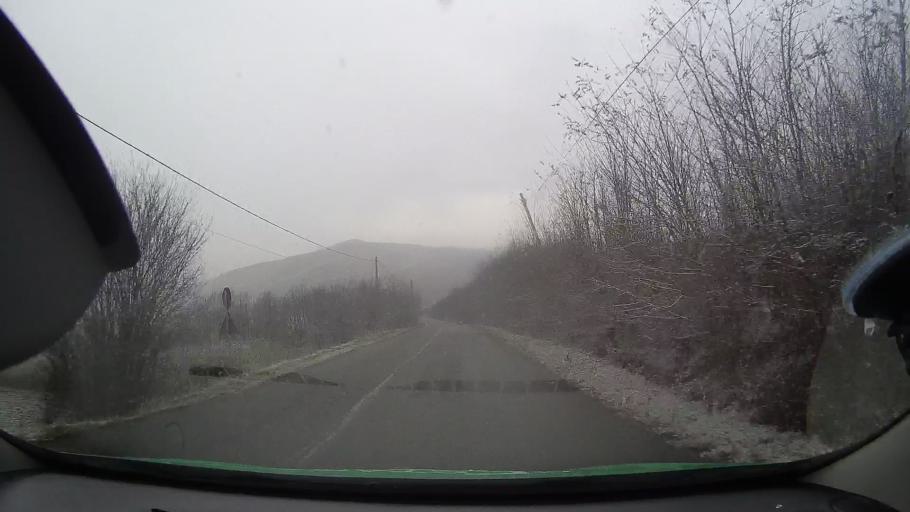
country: RO
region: Alba
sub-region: Comuna Noslac
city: Noslac
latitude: 46.3628
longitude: 23.9318
